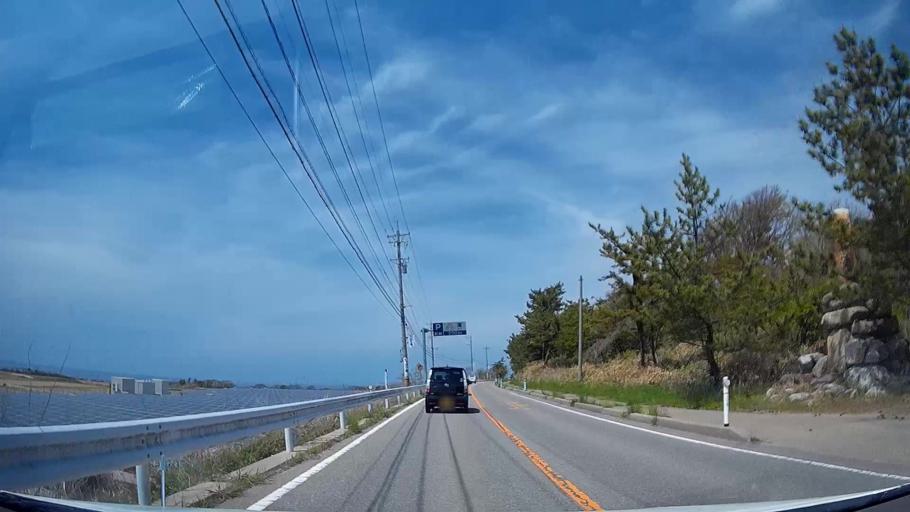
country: JP
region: Ishikawa
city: Hakui
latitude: 36.9303
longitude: 136.7564
